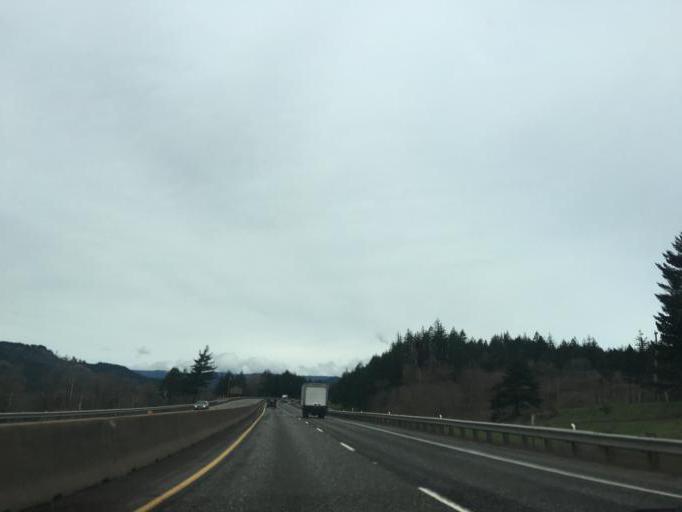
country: US
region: Washington
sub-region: Skamania County
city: Carson
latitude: 45.6880
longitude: -121.8396
